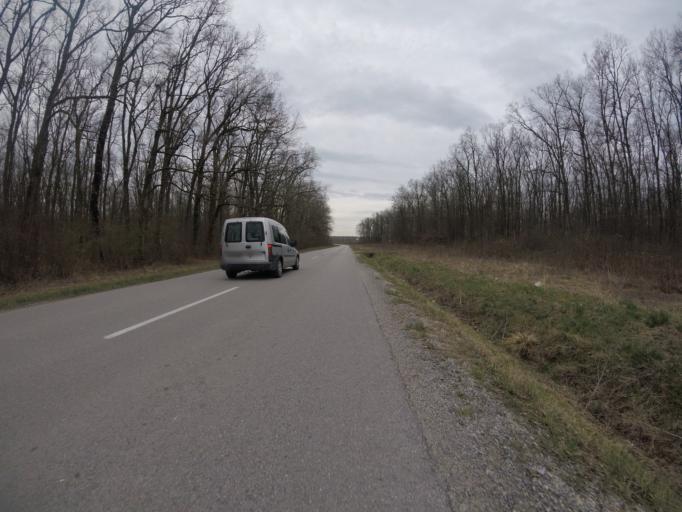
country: HR
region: Zagrebacka
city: Lukavec
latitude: 45.6911
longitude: 15.9818
